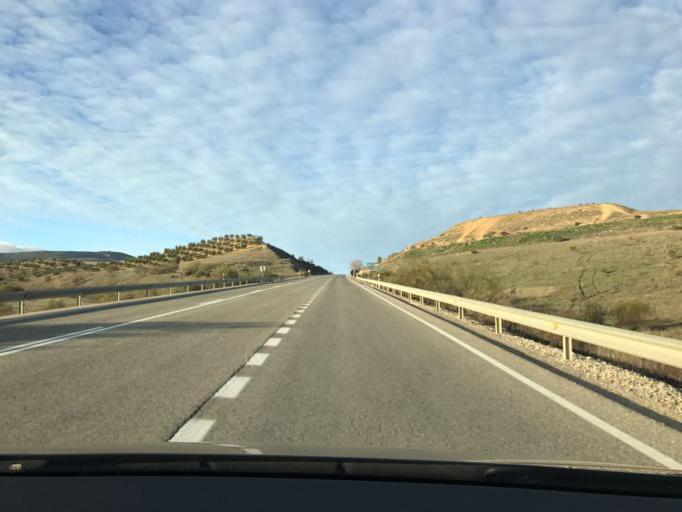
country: ES
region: Andalusia
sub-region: Provincia de Jaen
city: Guadahortuna
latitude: 37.5652
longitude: -3.4012
